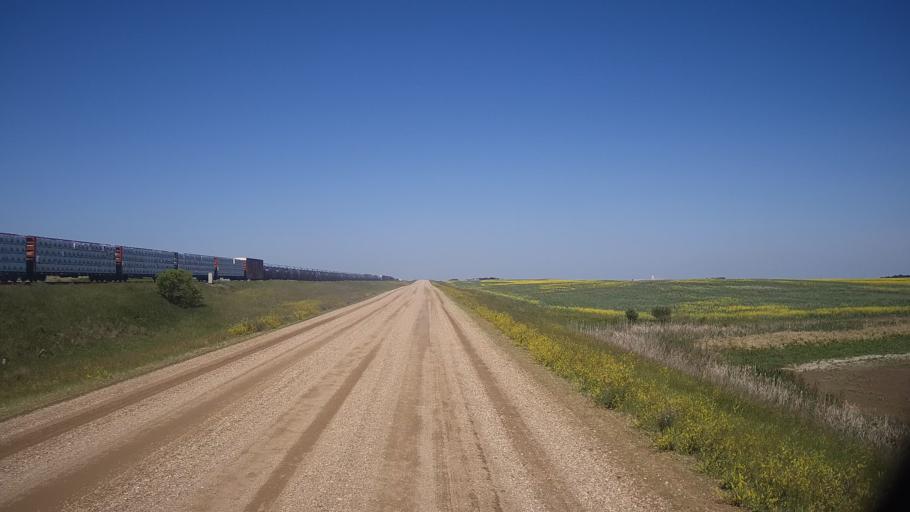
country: CA
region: Saskatchewan
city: Watrous
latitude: 51.8561
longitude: -105.9504
